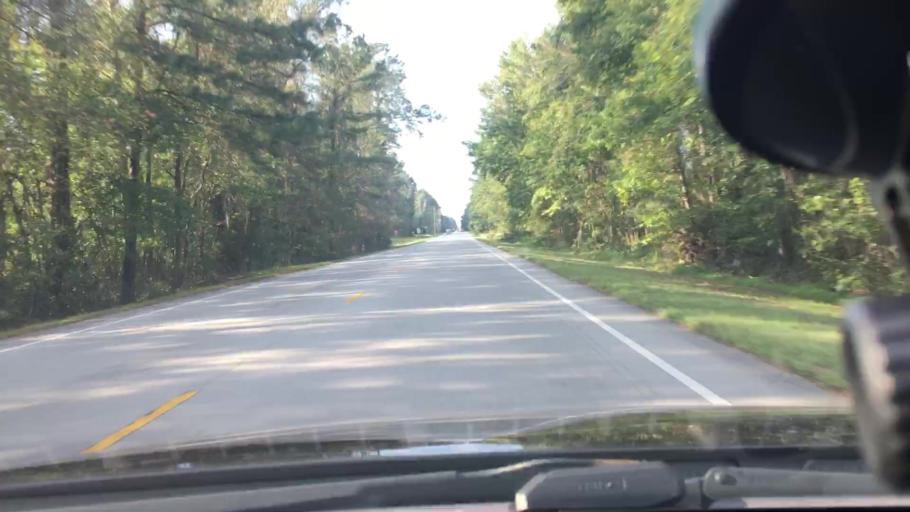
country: US
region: North Carolina
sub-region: Craven County
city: New Bern
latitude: 35.1932
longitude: -77.0533
